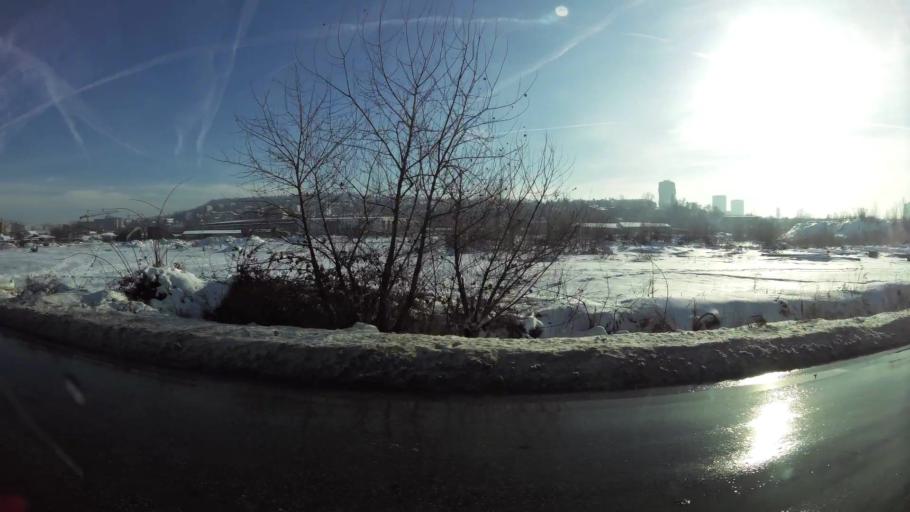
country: RS
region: Central Serbia
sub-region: Belgrade
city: Palilula
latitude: 44.8220
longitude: 20.4942
